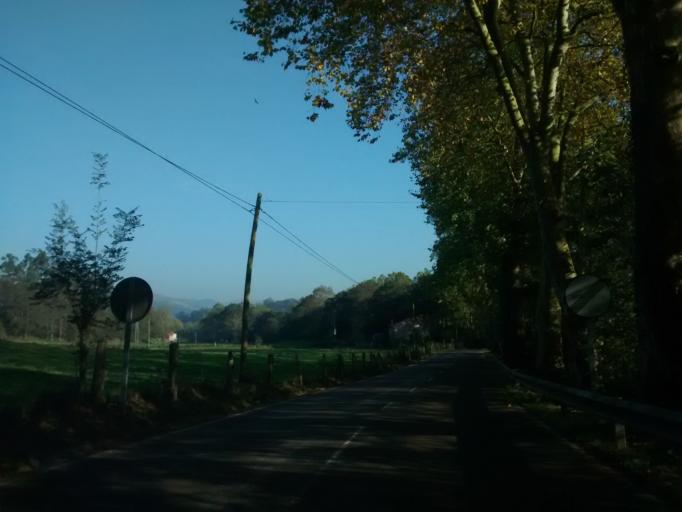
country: ES
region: Cantabria
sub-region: Provincia de Cantabria
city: Lierganes
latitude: 43.3495
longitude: -3.7254
